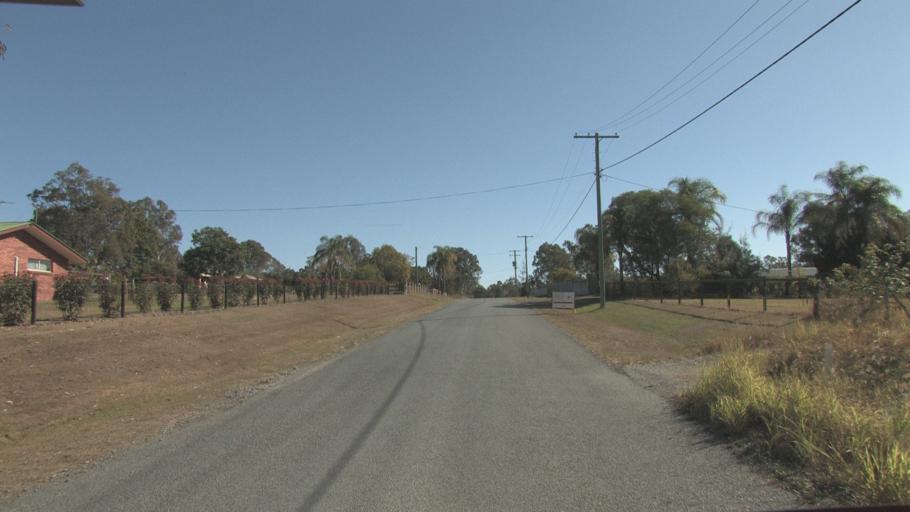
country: AU
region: Queensland
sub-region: Logan
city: Cedar Vale
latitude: -27.8526
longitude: 153.0203
